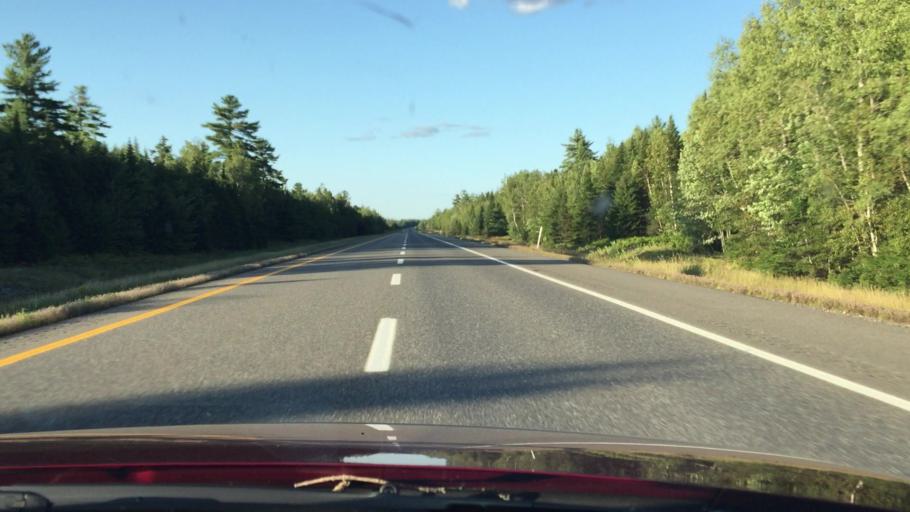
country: US
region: Maine
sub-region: Penobscot County
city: Patten
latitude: 46.0707
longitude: -68.2228
